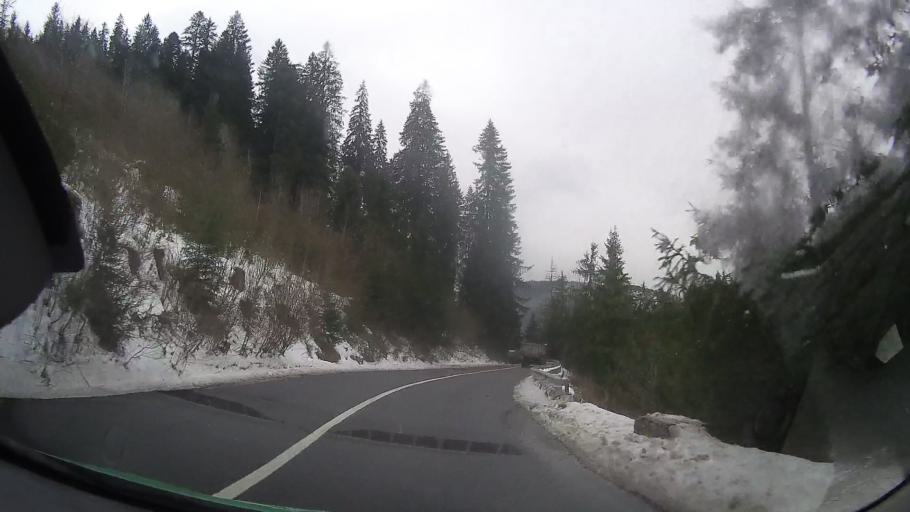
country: RO
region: Harghita
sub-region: Municipiul Gheorgheni
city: Gheorgheni
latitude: 46.7727
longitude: 25.7133
